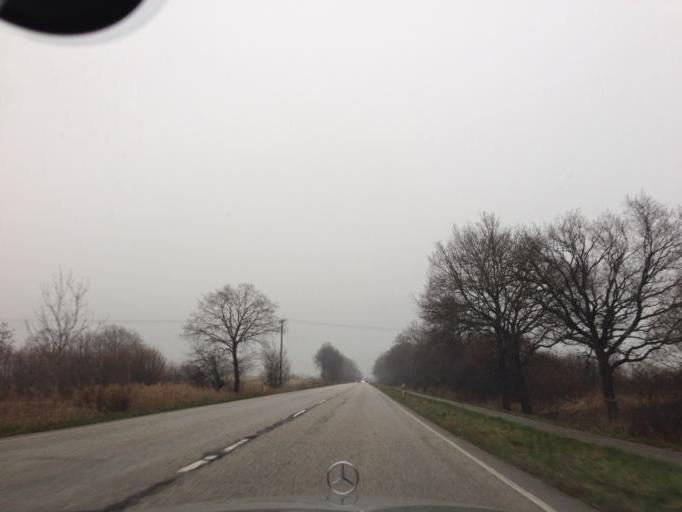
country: DE
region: Schleswig-Holstein
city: Klein Barkau
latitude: 54.2335
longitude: 10.1462
